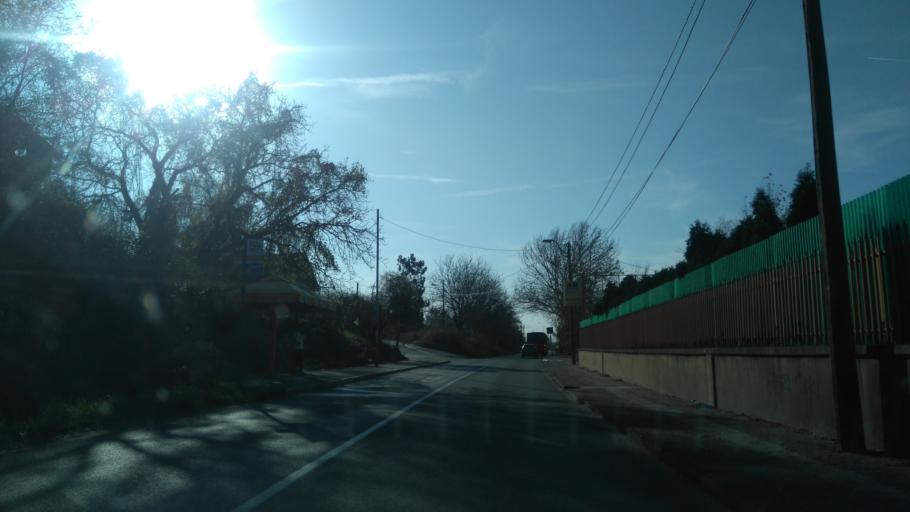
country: RS
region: Central Serbia
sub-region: Belgrade
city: Cukarica
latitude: 44.7469
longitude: 20.3972
